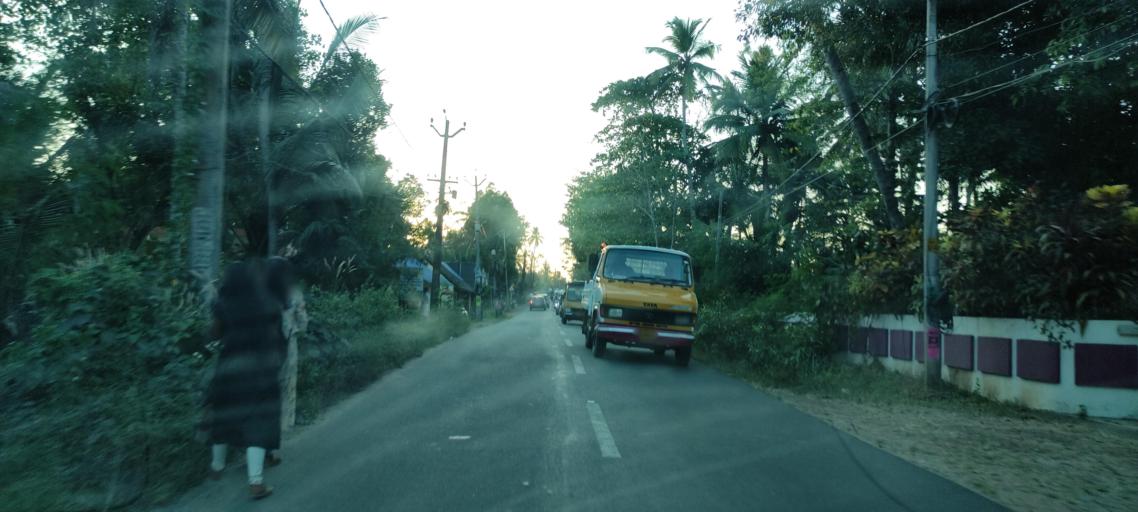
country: IN
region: Kerala
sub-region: Alappuzha
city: Kayankulam
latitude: 9.2590
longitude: 76.4347
